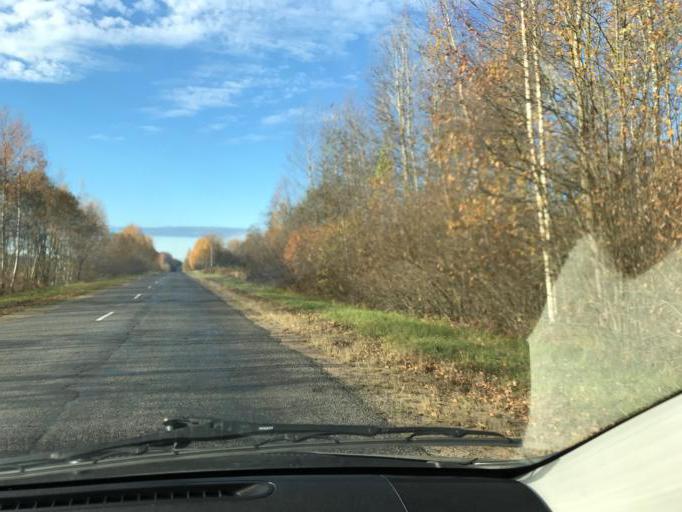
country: BY
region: Vitebsk
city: Haradok
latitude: 55.4021
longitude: 29.7220
